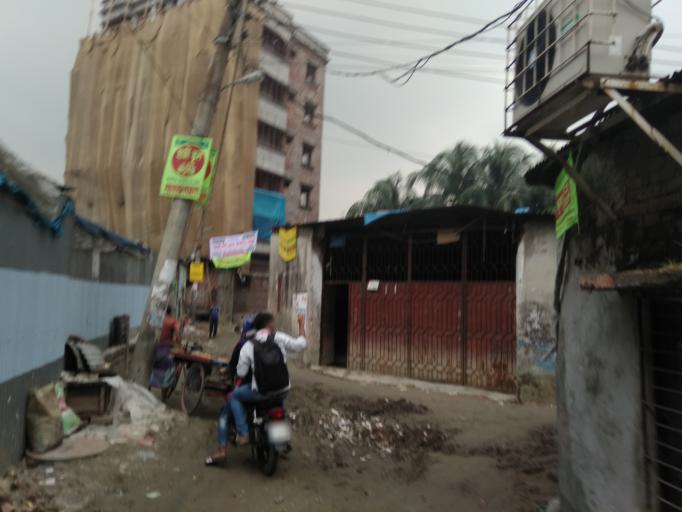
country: BD
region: Dhaka
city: Paltan
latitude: 23.7837
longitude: 90.4295
